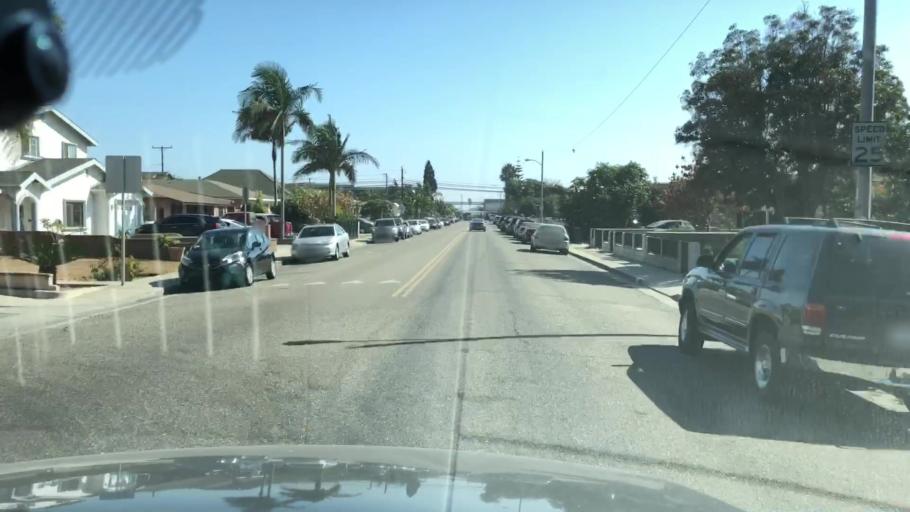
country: US
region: California
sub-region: Ventura County
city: Oxnard
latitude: 34.2027
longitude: -119.1685
